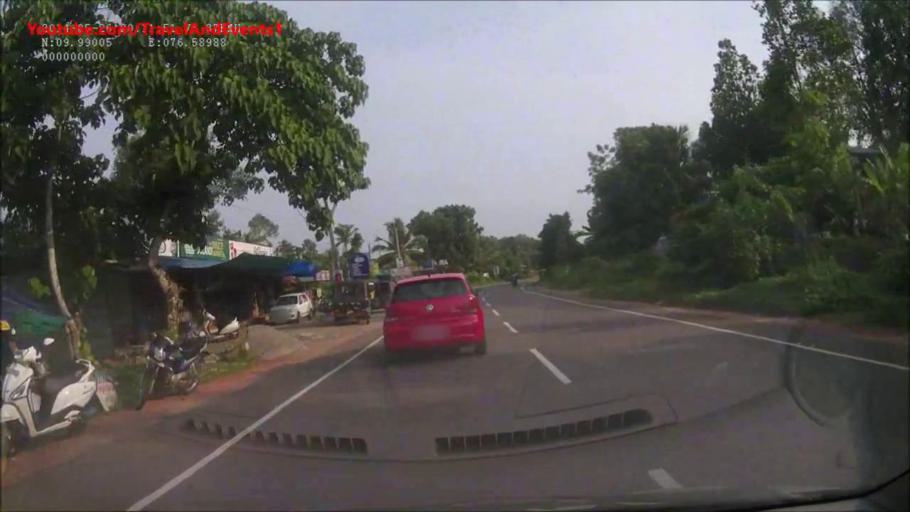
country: IN
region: Kerala
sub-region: Ernakulam
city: Muvattupula
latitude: 9.9892
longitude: 76.5897
